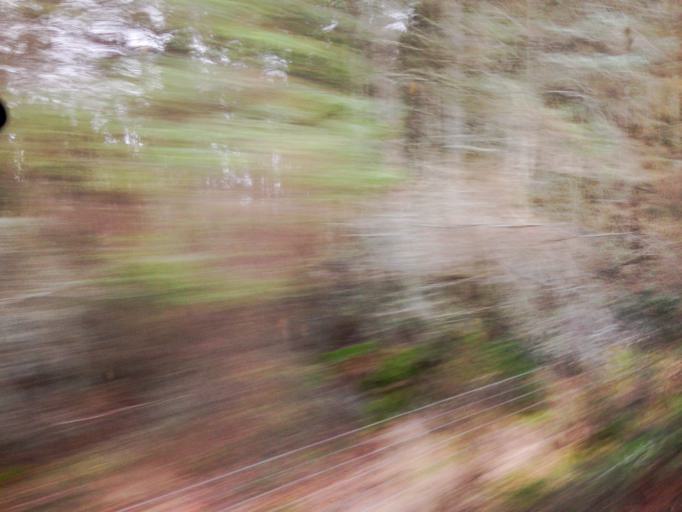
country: GB
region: Scotland
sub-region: Highland
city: Fort William
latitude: 56.8449
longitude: -5.1544
